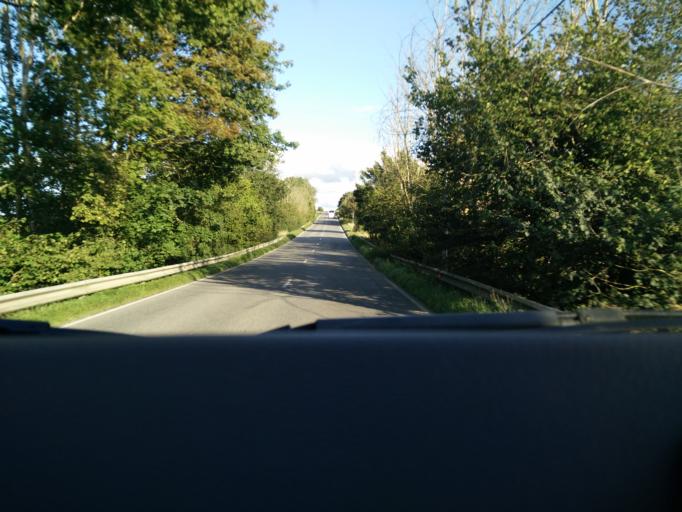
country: BE
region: Wallonia
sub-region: Province de Namur
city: Walcourt
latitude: 50.2187
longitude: 4.4389
